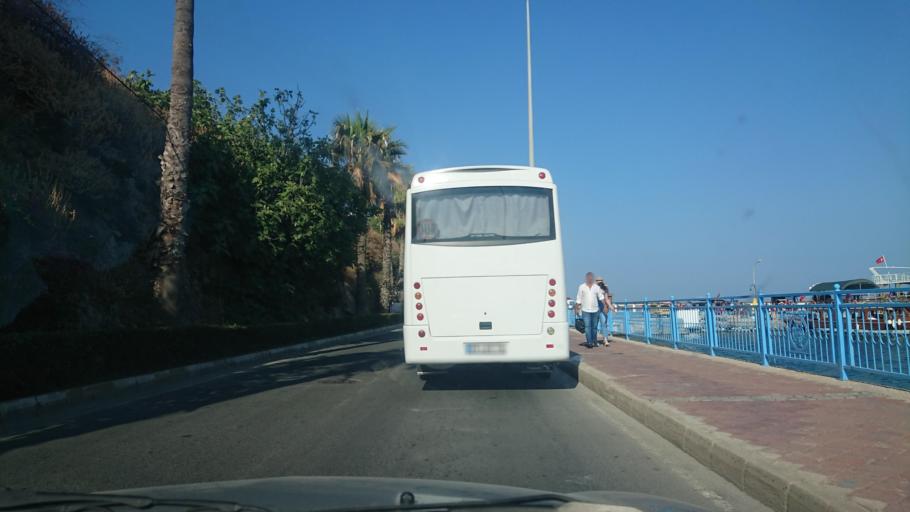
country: TR
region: Aydin
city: Kusadasi
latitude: 37.8612
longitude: 27.2507
